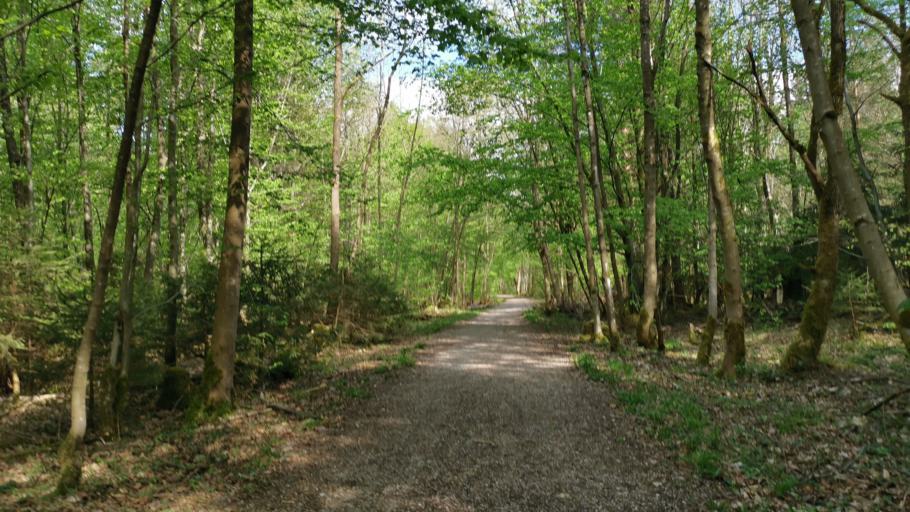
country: DE
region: Bavaria
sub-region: Upper Bavaria
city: Neuried
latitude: 48.0759
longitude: 11.4780
